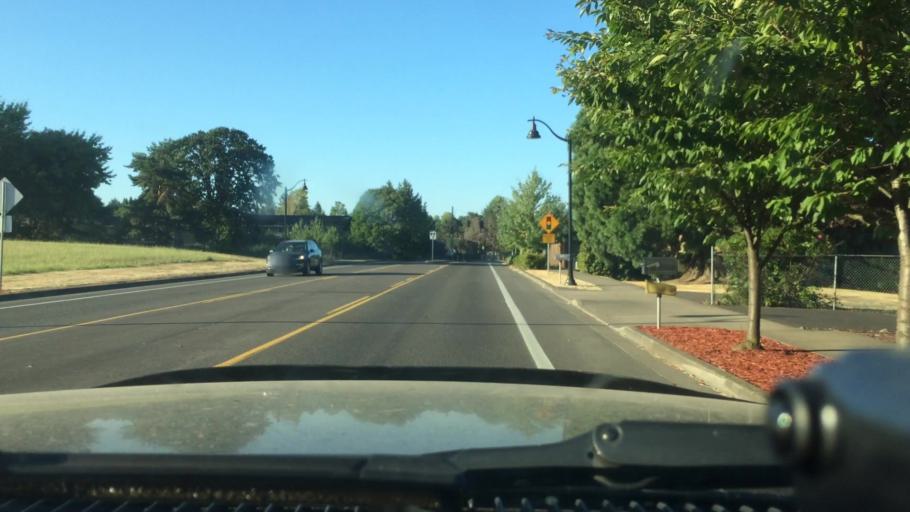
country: US
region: Oregon
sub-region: Yamhill County
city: Newberg
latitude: 45.3146
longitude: -122.9458
